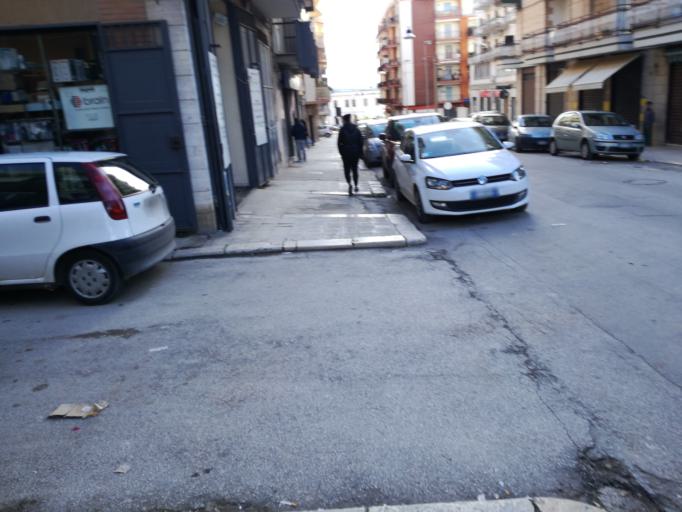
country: IT
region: Apulia
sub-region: Provincia di Bari
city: Ruvo di Puglia
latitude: 41.1164
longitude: 16.4803
